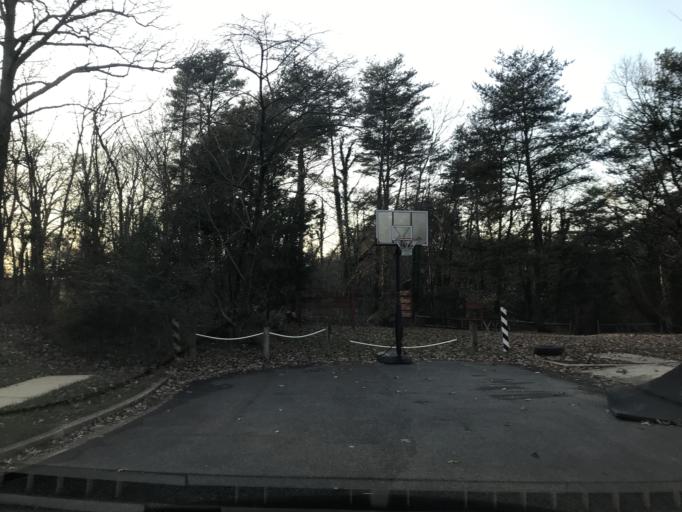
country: US
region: Virginia
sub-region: Fairfax County
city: Franconia
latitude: 38.7885
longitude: -77.1661
